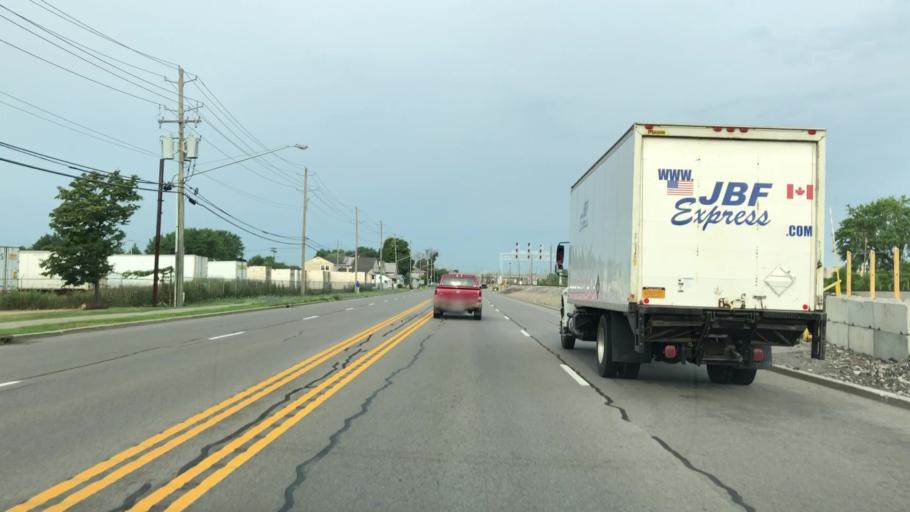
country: US
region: New York
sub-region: Erie County
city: Cheektowaga
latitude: 42.9018
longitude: -78.7737
